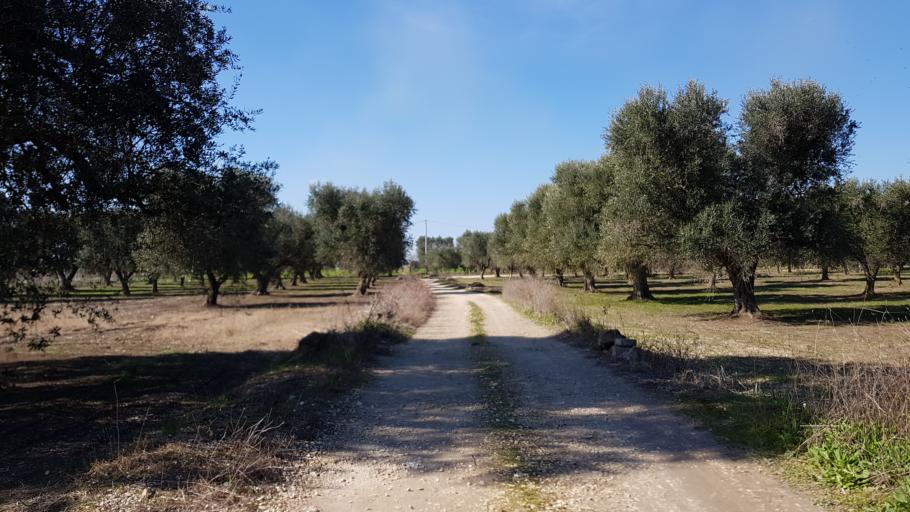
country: IT
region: Apulia
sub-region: Provincia di Brindisi
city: Mesagne
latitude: 40.6179
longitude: 17.8025
